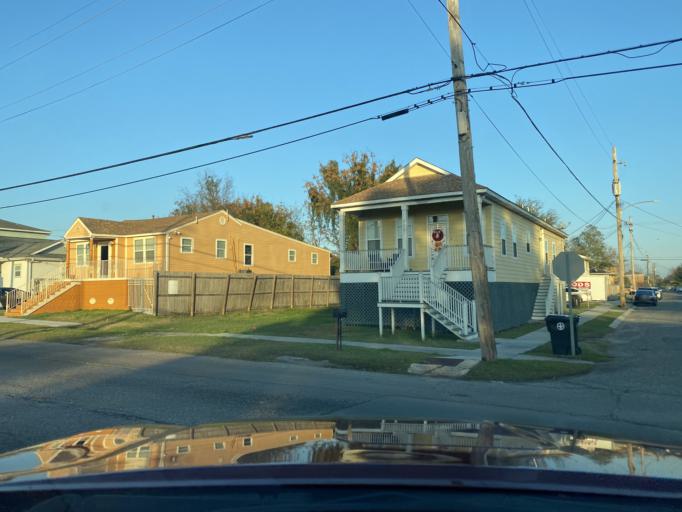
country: US
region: Louisiana
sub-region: Orleans Parish
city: New Orleans
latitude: 30.0184
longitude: -90.0515
